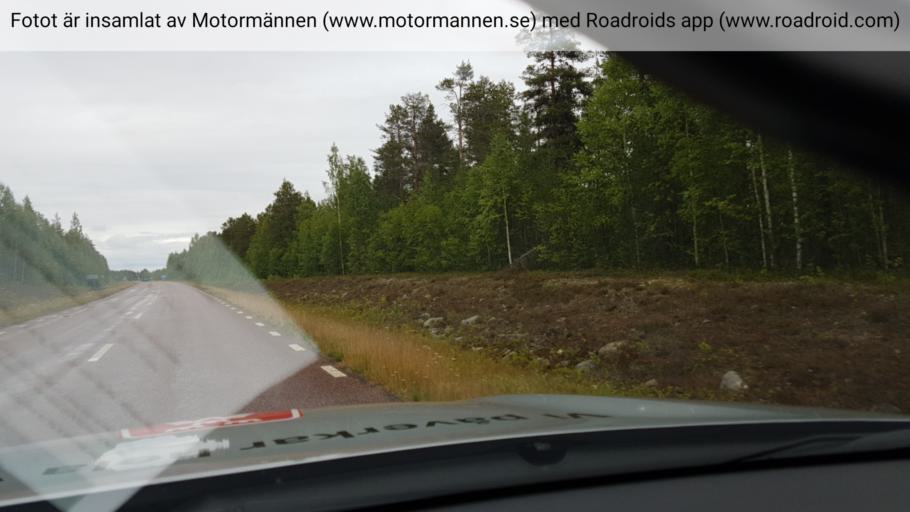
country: SE
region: Norrbotten
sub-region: Pajala Kommun
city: Pajala
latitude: 67.1523
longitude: 22.6285
